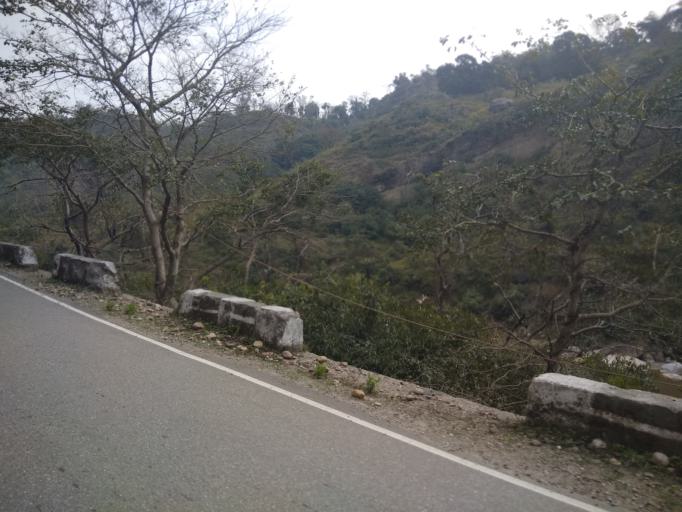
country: IN
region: Himachal Pradesh
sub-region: Kangra
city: Kotla
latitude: 32.2258
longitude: 76.0623
